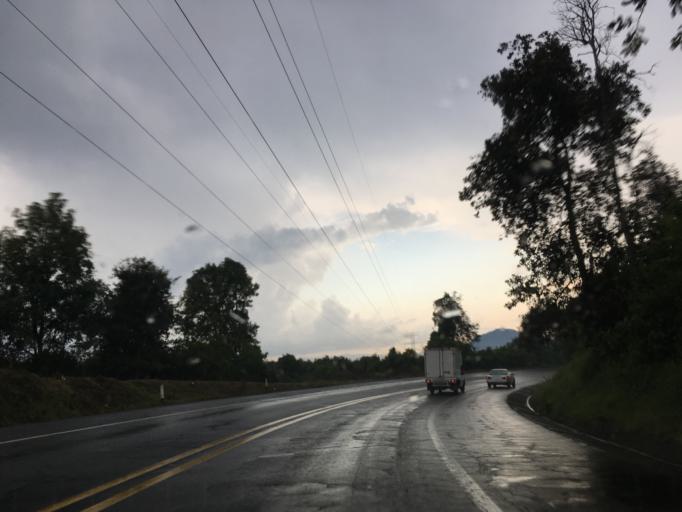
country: MX
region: Michoacan
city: Capacuaro
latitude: 19.5181
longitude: -102.0752
